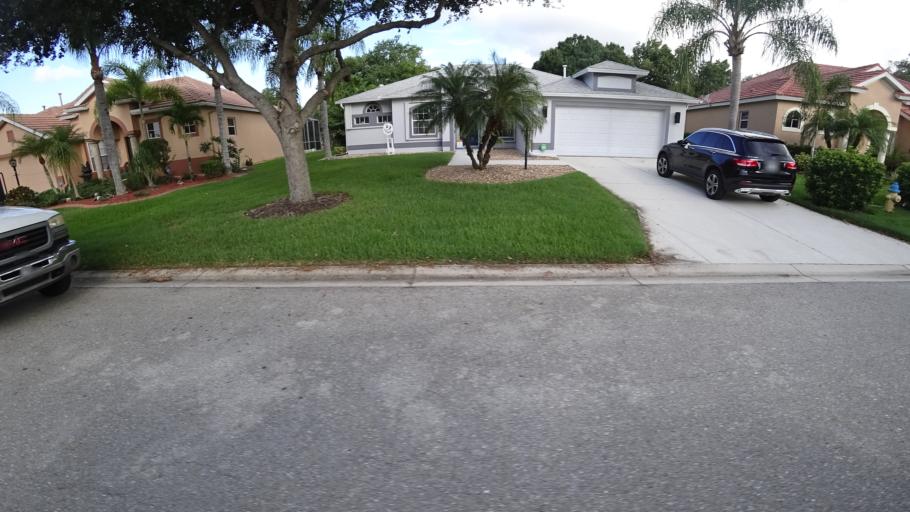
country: US
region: Florida
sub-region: Sarasota County
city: North Sarasota
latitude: 27.4211
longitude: -82.5005
